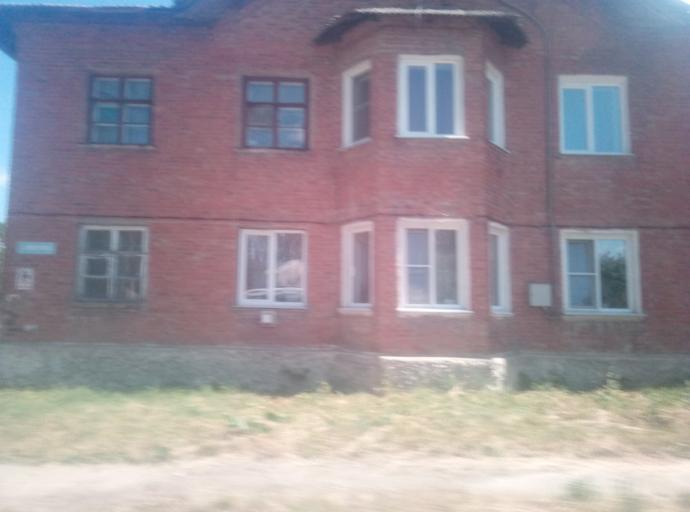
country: RU
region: Tula
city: Kireyevsk
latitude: 53.9261
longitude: 37.9224
